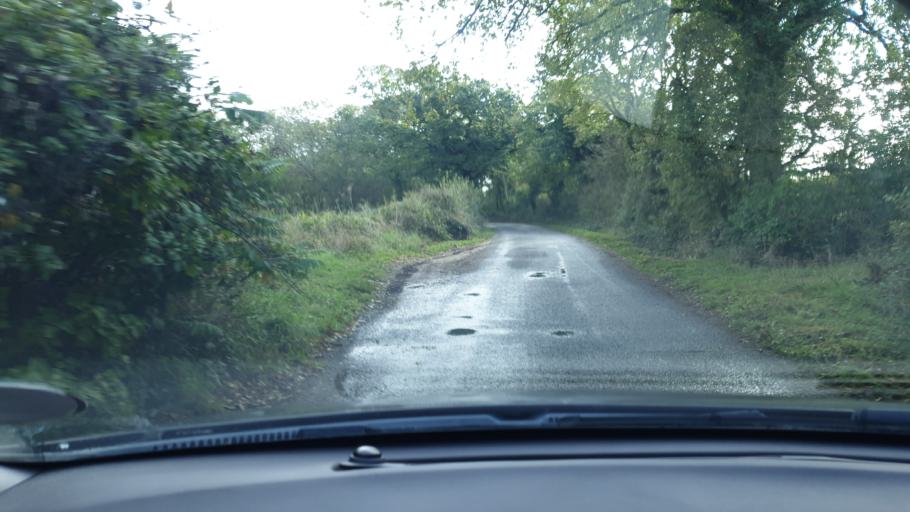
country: GB
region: England
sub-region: Essex
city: Alresford
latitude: 51.8579
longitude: 1.0303
